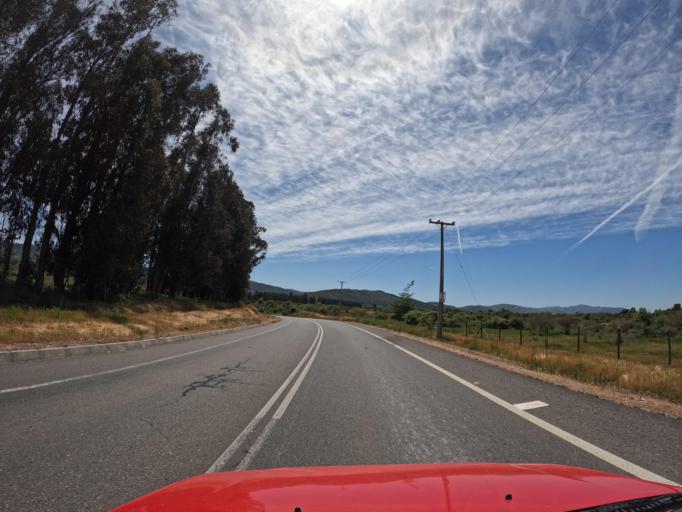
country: CL
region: Maule
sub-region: Provincia de Talca
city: Talca
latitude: -35.2821
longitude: -71.5307
